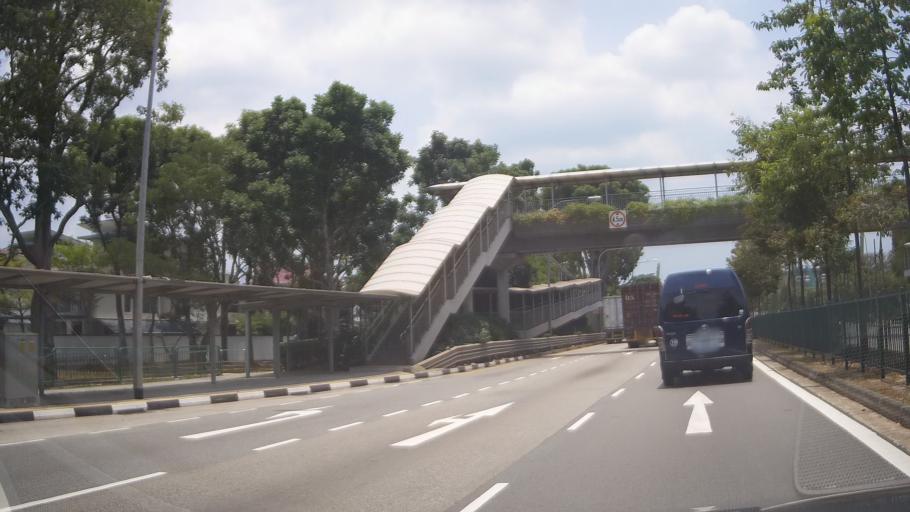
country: SG
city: Singapore
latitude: 1.2953
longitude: 103.7652
